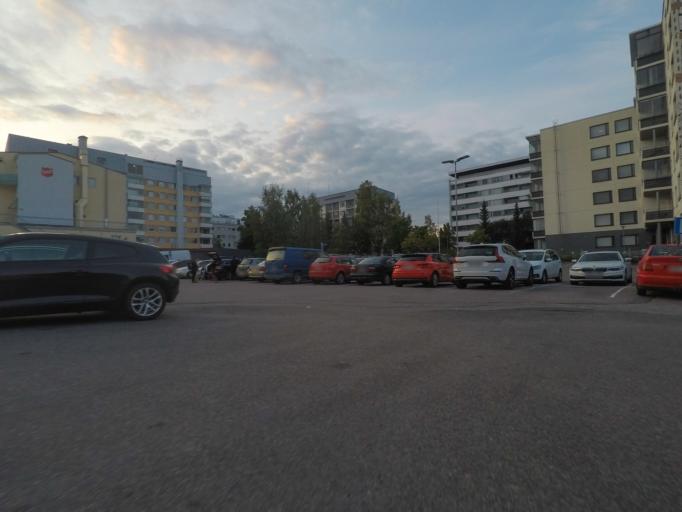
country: FI
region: Central Finland
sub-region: Jyvaeskylae
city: Jyvaeskylae
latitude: 62.2434
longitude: 25.7524
